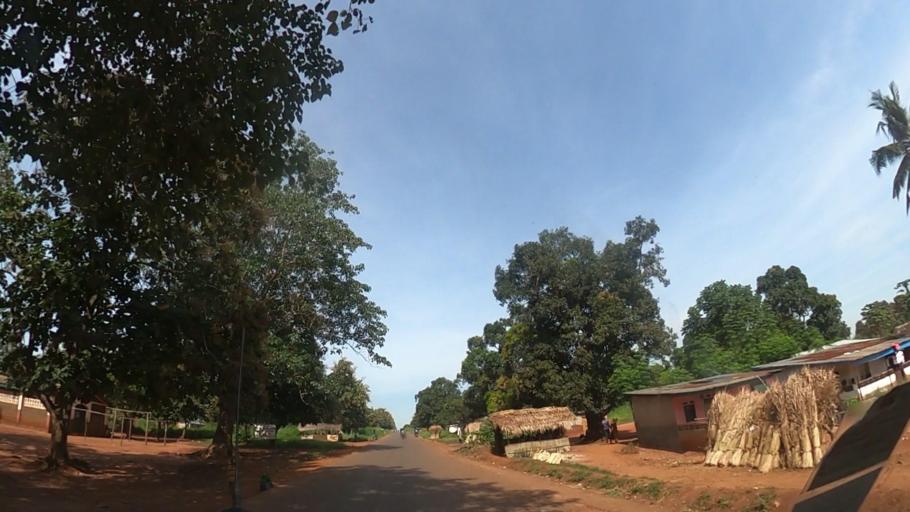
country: CF
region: Ombella-Mpoko
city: Bimbo
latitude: 4.3124
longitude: 18.4774
